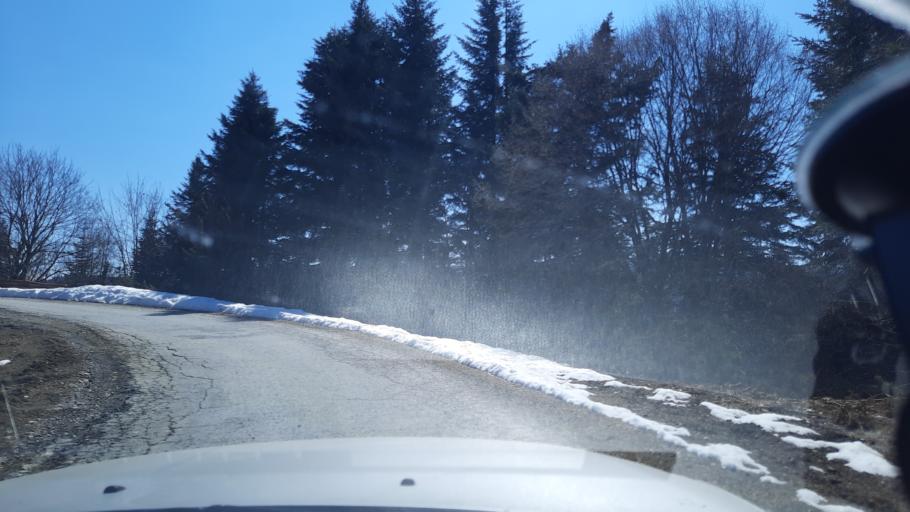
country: MK
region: Gostivar
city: Vrutok
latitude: 41.7132
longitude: 20.7259
